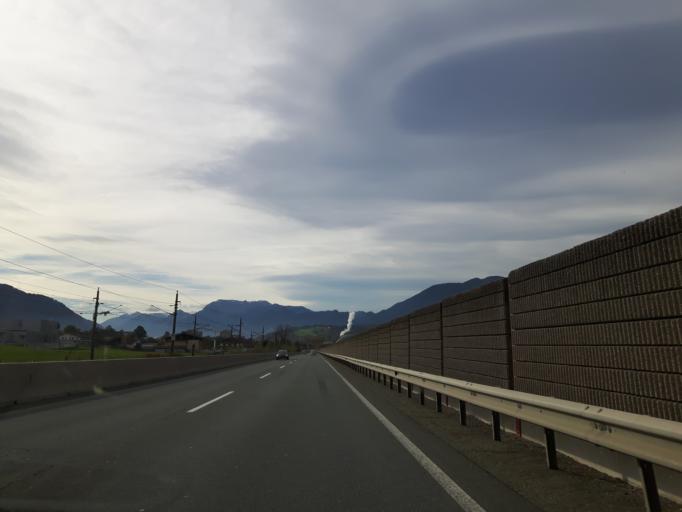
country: AT
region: Tyrol
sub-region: Politischer Bezirk Kufstein
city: Angath
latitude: 47.4931
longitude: 12.0803
